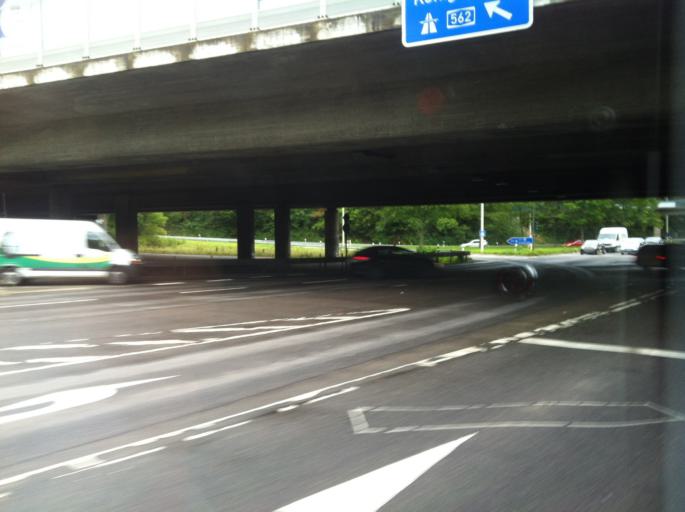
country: DE
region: North Rhine-Westphalia
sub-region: Regierungsbezirk Koln
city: Bonn
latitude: 50.7111
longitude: 7.1382
